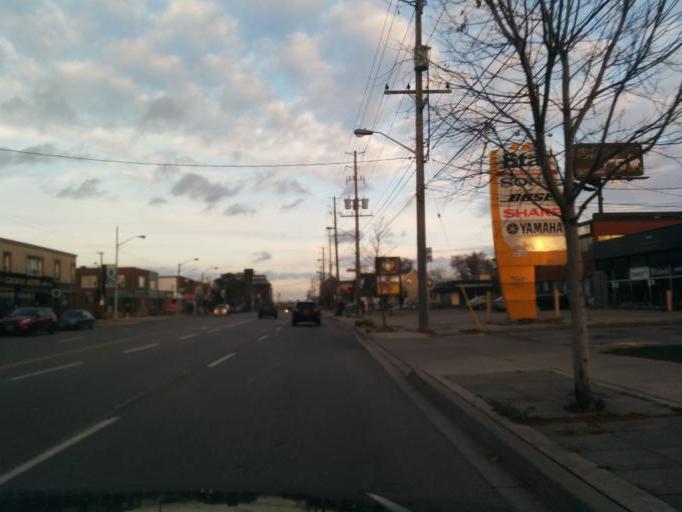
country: CA
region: Ontario
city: Etobicoke
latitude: 43.6247
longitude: -79.5096
